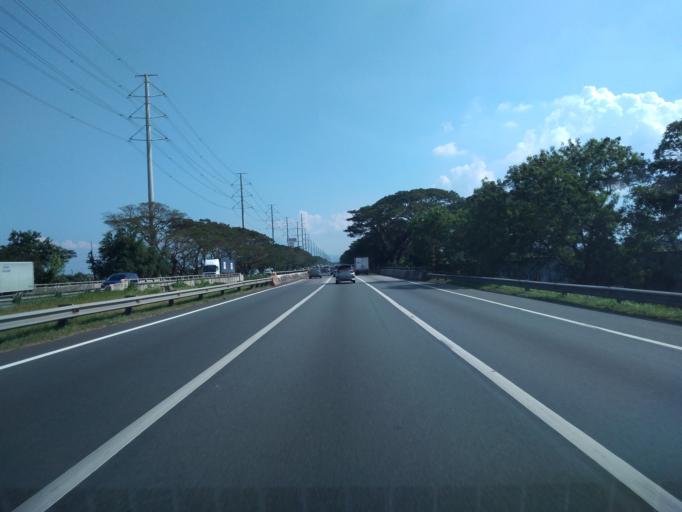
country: PH
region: Calabarzon
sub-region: Province of Laguna
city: Pulong Santa Cruz
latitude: 14.2718
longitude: 121.0952
